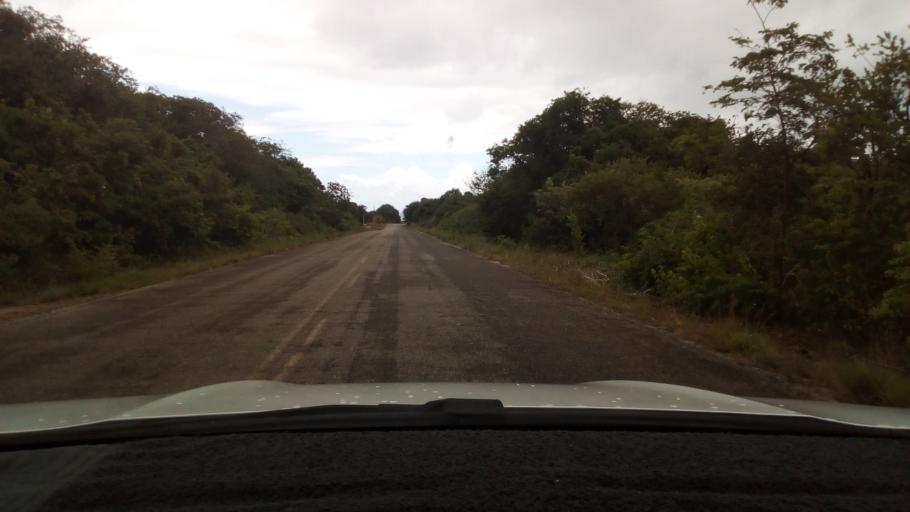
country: BR
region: Paraiba
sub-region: Pitimbu
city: Pitimbu
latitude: -7.3609
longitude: -34.8048
